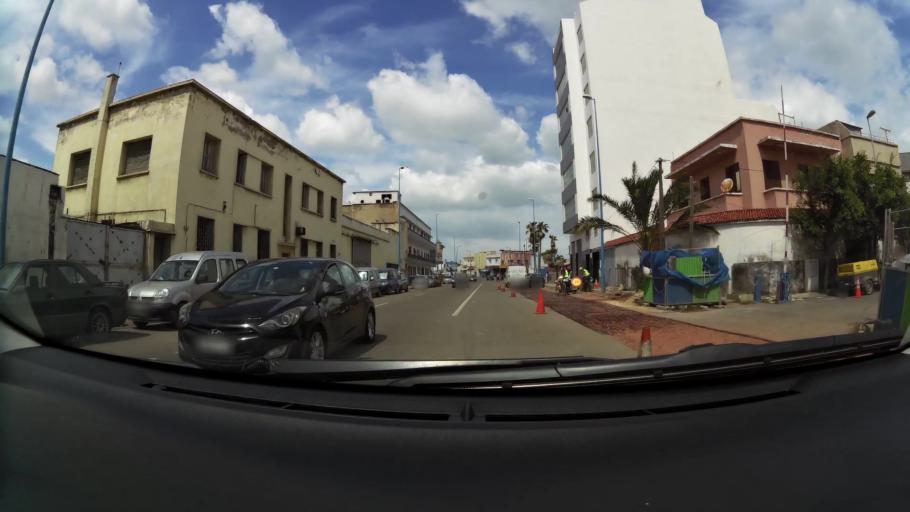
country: MA
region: Grand Casablanca
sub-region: Casablanca
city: Casablanca
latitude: 33.6178
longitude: -7.5428
